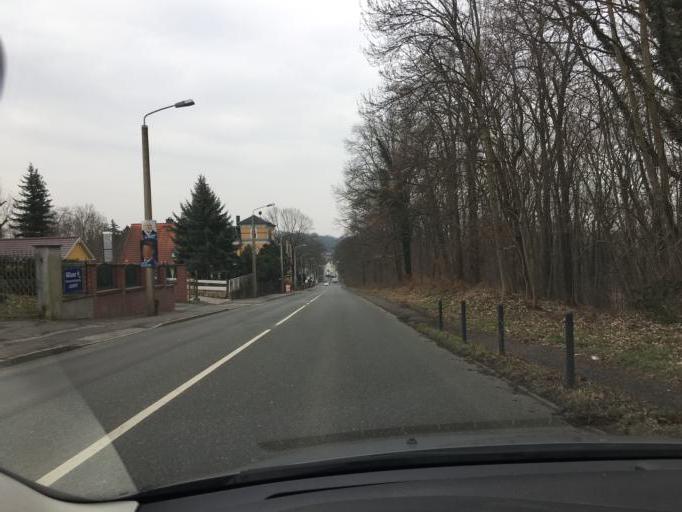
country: DE
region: Thuringia
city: Altenburg
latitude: 51.0001
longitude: 12.4497
